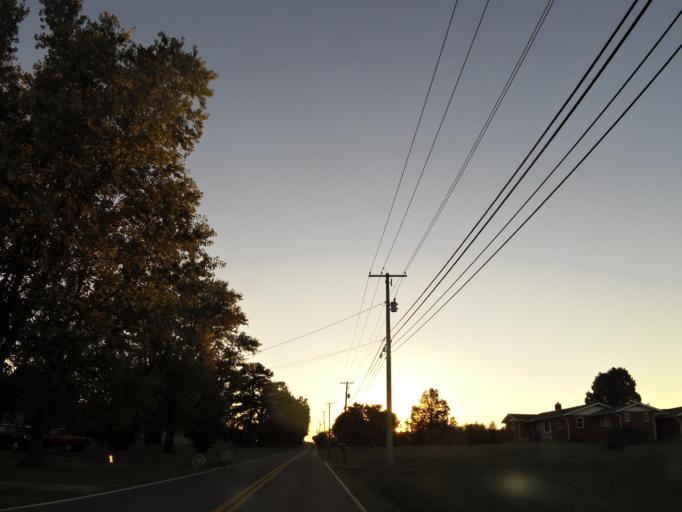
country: US
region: Tennessee
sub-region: Union County
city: Condon
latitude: 36.1521
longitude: -83.7698
